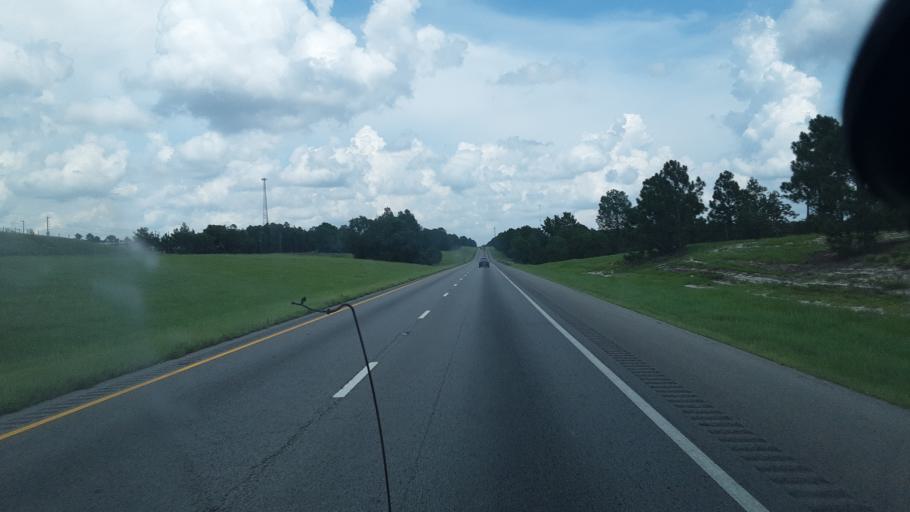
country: US
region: South Carolina
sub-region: Kershaw County
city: Elgin
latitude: 34.1588
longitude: -80.7273
